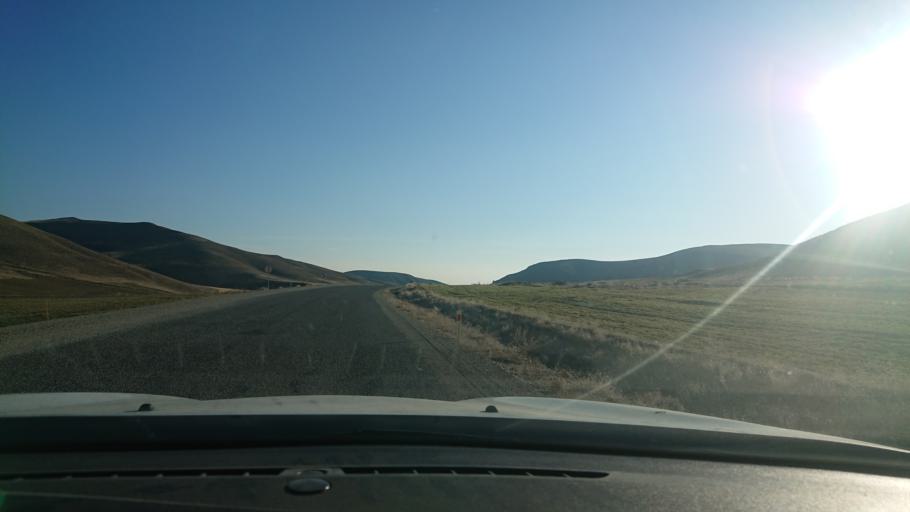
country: TR
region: Aksaray
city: Acipinar
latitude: 38.7033
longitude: 33.7547
